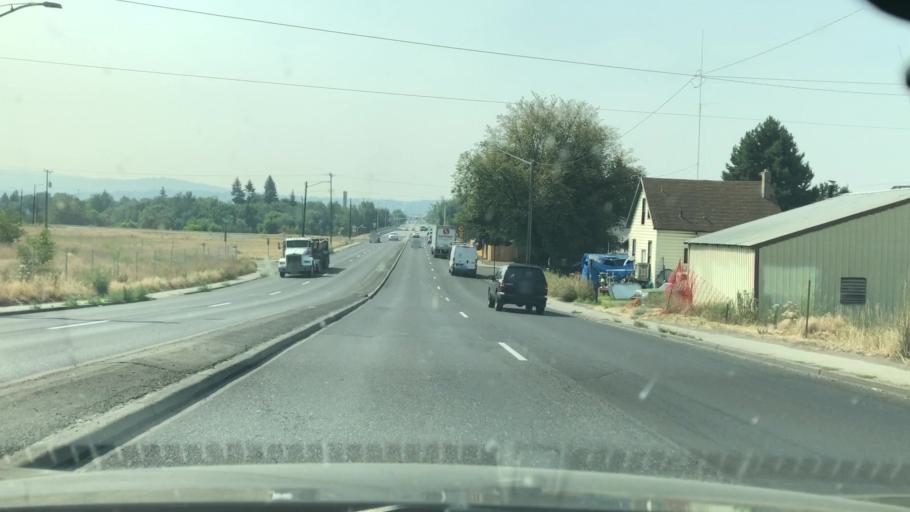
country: US
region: Washington
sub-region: Spokane County
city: Spokane
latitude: 47.6812
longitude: -117.3637
